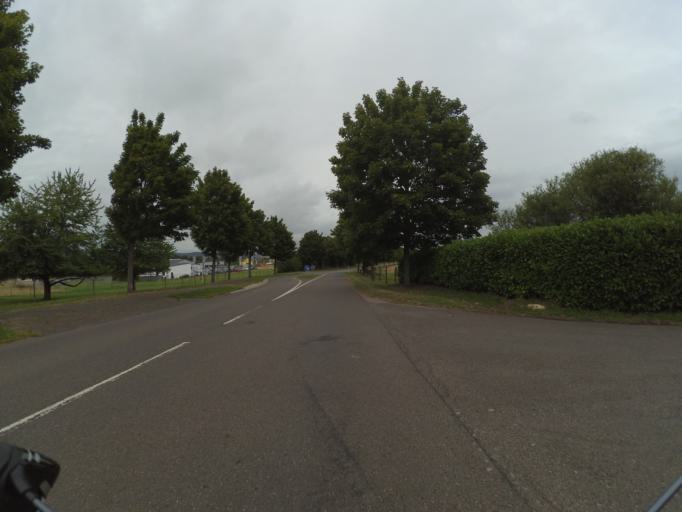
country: DE
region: Rheinland-Pfalz
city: Bekond
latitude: 49.8514
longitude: 6.8013
